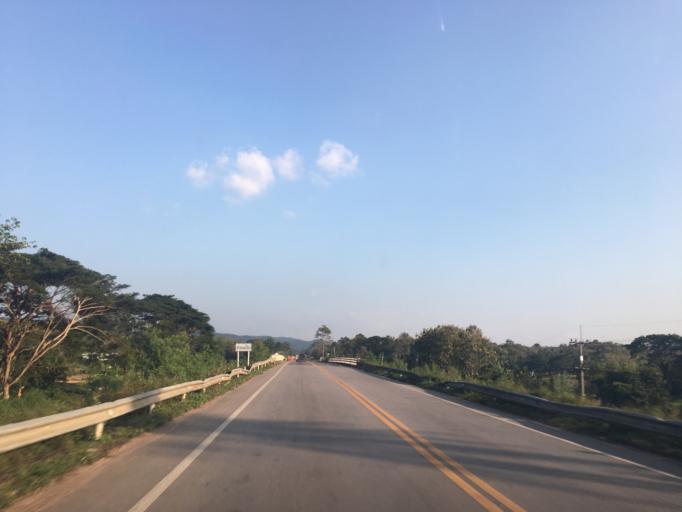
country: TH
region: Lampang
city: Ngao
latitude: 18.7163
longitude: 99.9791
